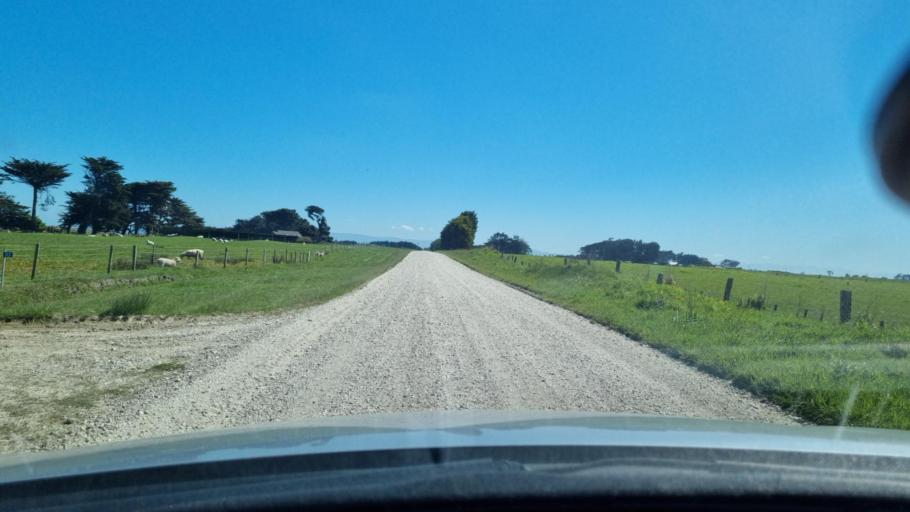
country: NZ
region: Southland
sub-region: Invercargill City
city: Invercargill
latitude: -46.4186
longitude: 168.2696
